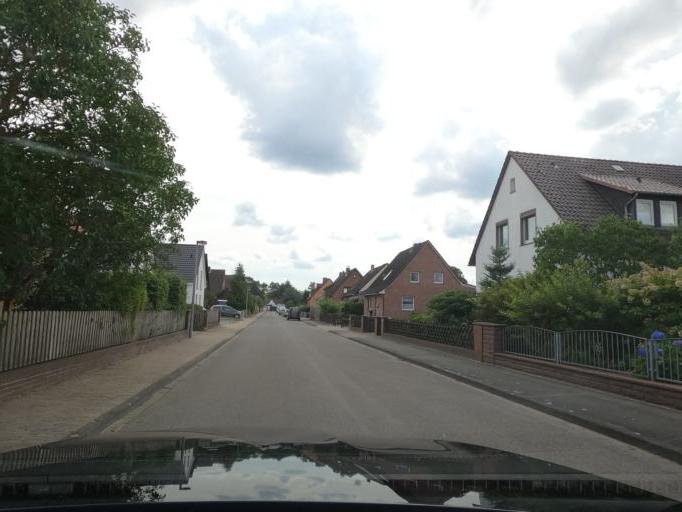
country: DE
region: Lower Saxony
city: Isernhagen Farster Bauerschaft
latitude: 52.5176
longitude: 9.9179
